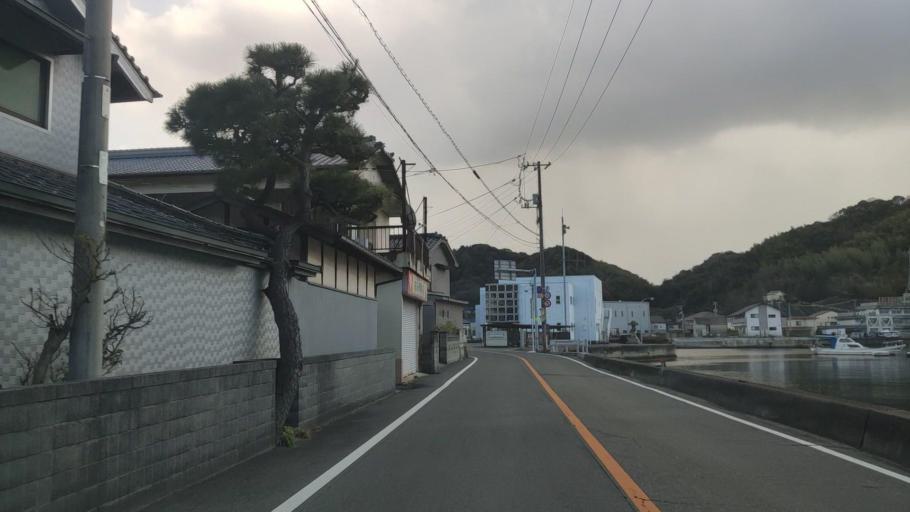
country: JP
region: Hiroshima
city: Innoshima
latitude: 34.2060
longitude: 133.1185
